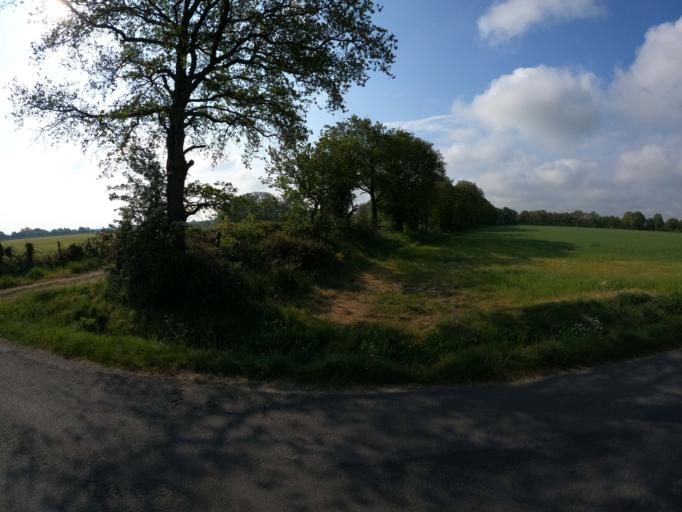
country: FR
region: Pays de la Loire
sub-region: Departement de Maine-et-Loire
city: La Romagne
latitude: 47.0646
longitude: -1.0379
